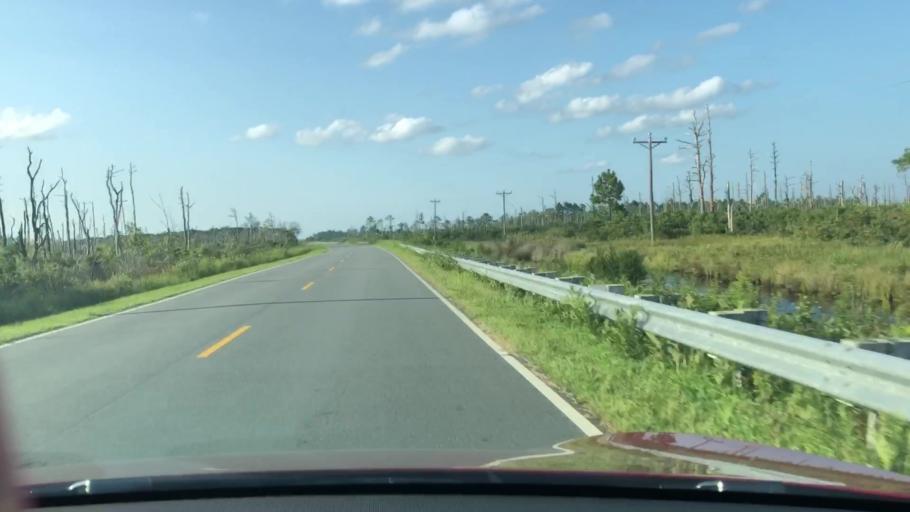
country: US
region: North Carolina
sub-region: Dare County
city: Wanchese
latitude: 35.6587
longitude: -75.7773
